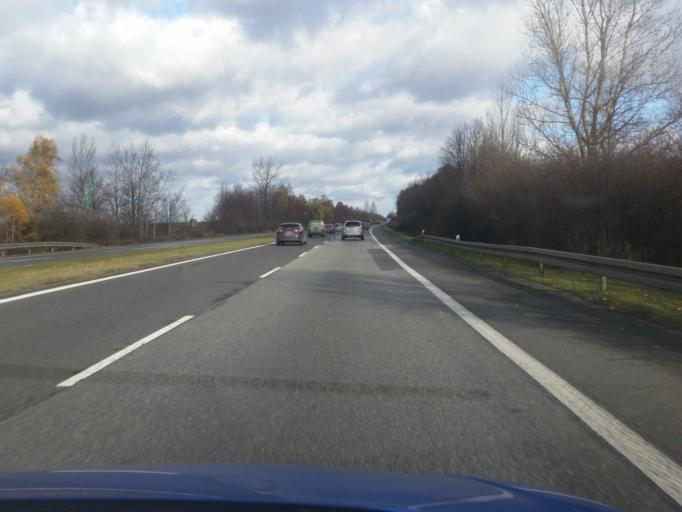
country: PL
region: Silesian Voivodeship
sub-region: Powiat czestochowski
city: Redziny
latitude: 50.8659
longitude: 19.1553
